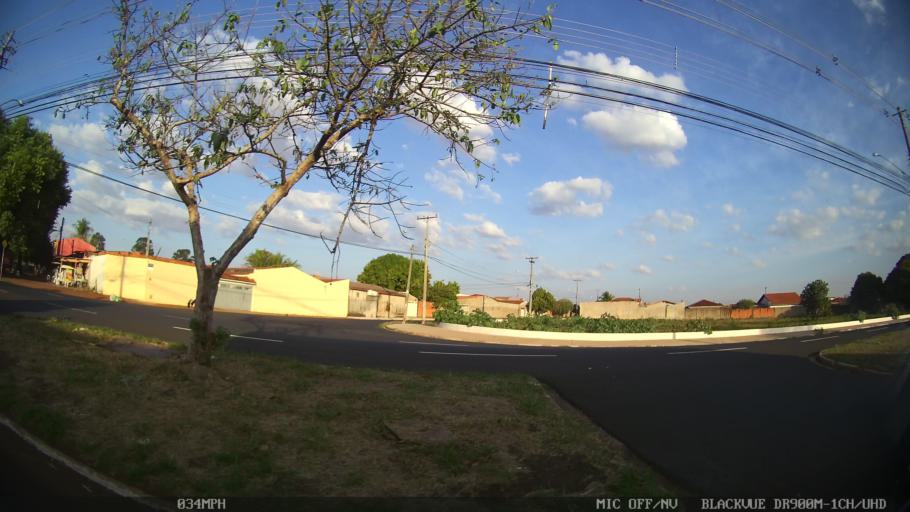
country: BR
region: Sao Paulo
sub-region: Ribeirao Preto
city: Ribeirao Preto
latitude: -21.1661
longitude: -47.7473
